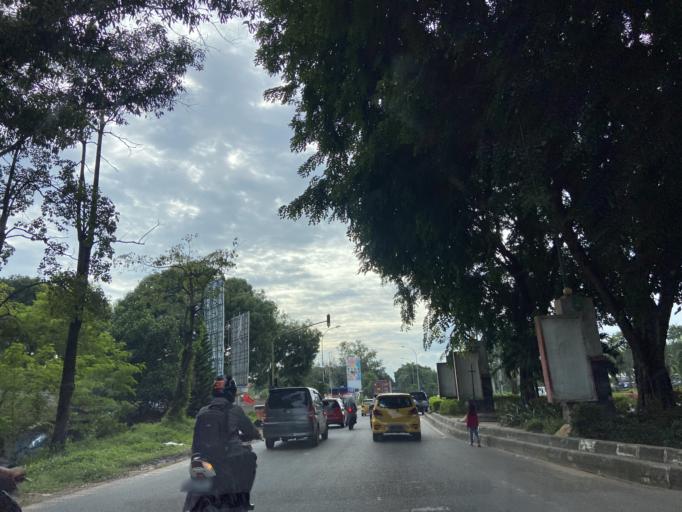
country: SG
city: Singapore
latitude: 1.1048
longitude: 103.9556
